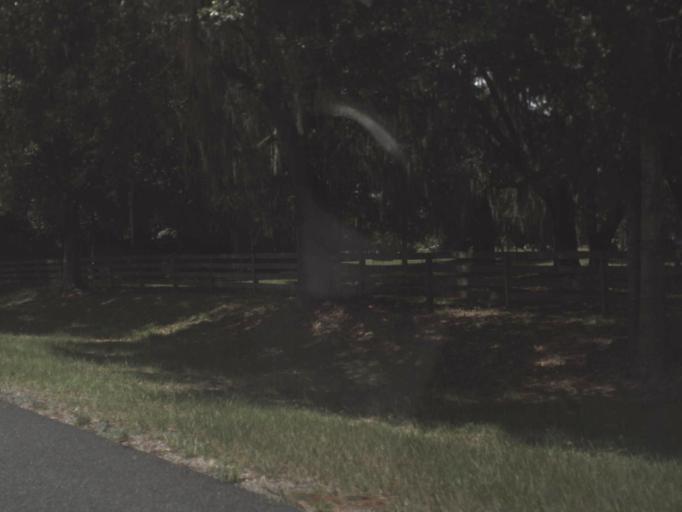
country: US
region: Florida
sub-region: Taylor County
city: Perry
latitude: 30.1758
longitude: -83.6345
